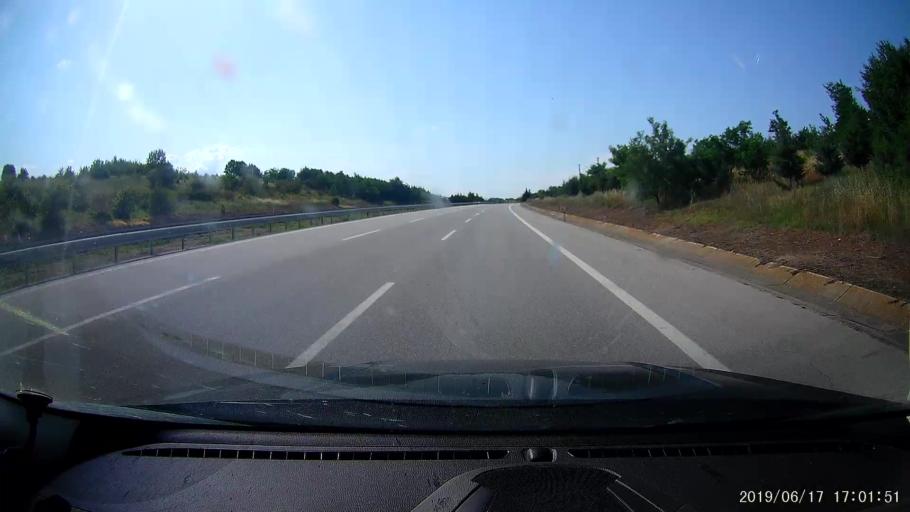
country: TR
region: Edirne
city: Haskoy
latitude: 41.6328
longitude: 26.7947
